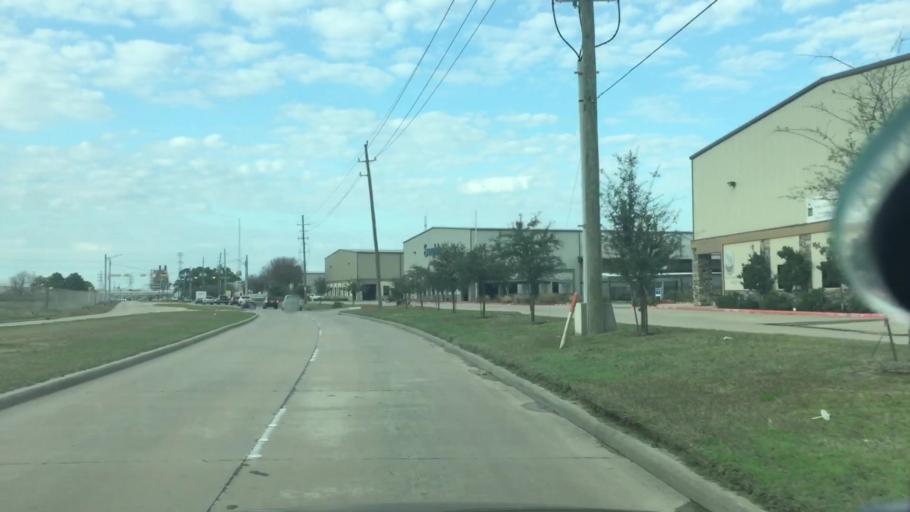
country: US
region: Texas
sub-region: Harris County
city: Hudson
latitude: 29.9286
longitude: -95.5255
